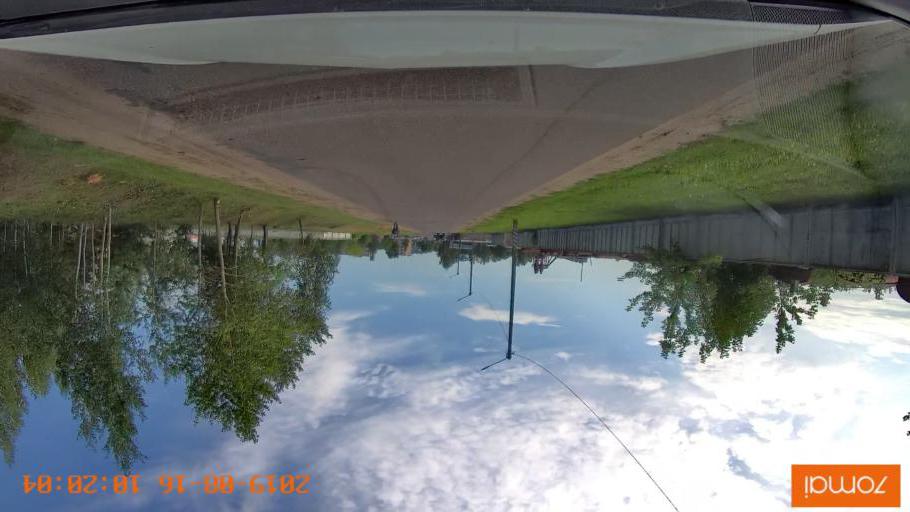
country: BY
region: Mogilev
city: Asipovichy
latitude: 53.3036
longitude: 28.6636
